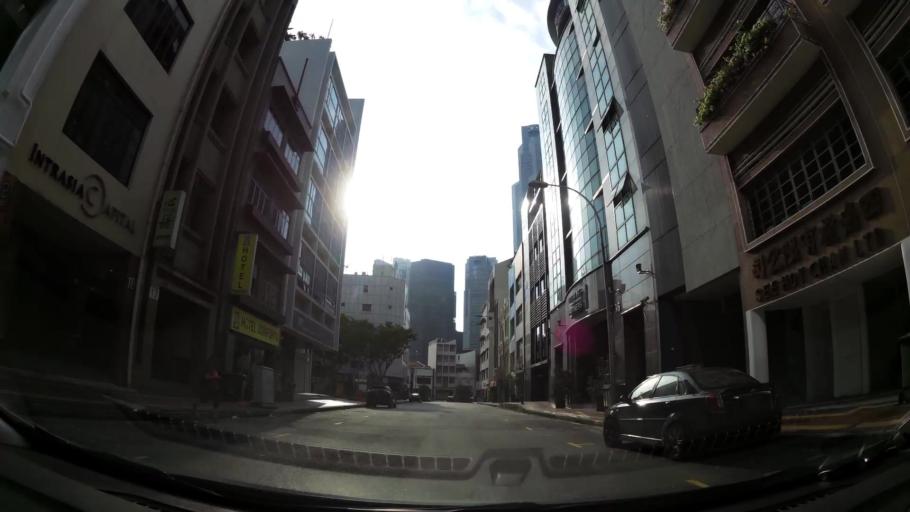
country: SG
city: Singapore
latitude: 1.2885
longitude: 103.8475
